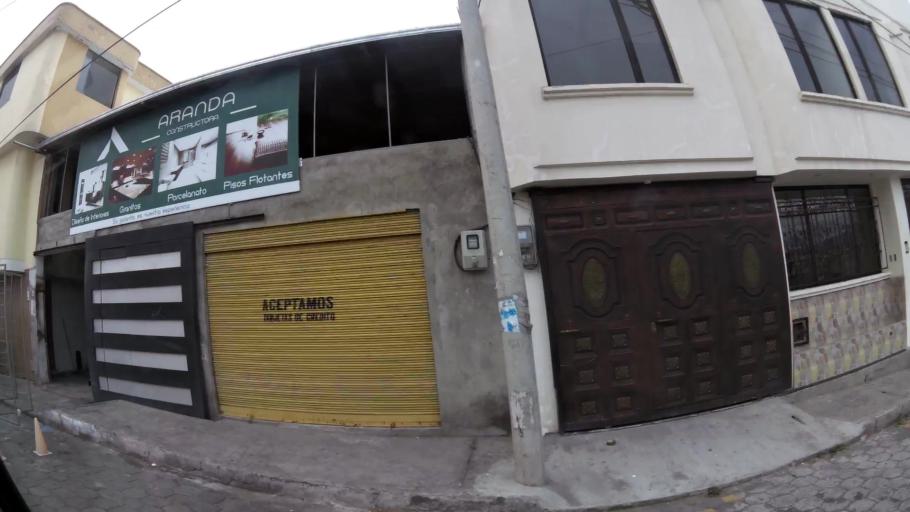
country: EC
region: Cotopaxi
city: Latacunga
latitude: -0.9316
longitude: -78.6106
